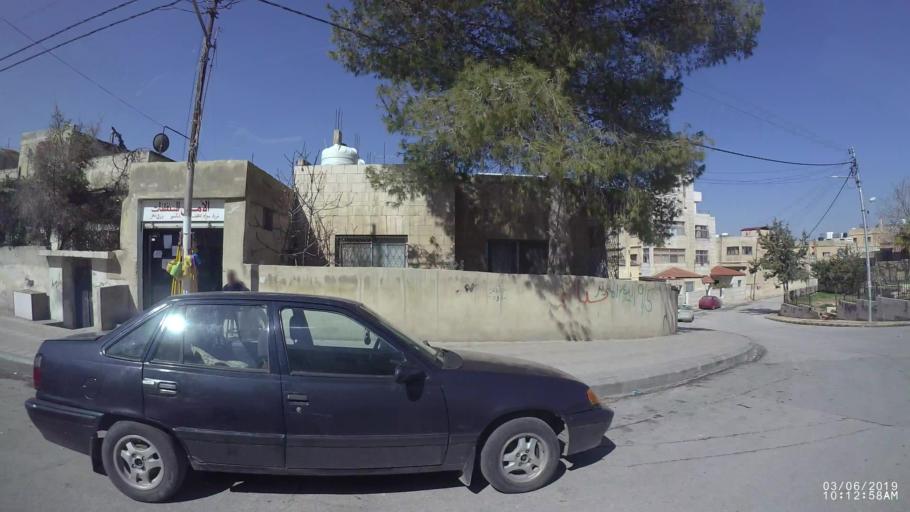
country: JO
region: Amman
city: Amman
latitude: 31.9812
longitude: 35.9847
